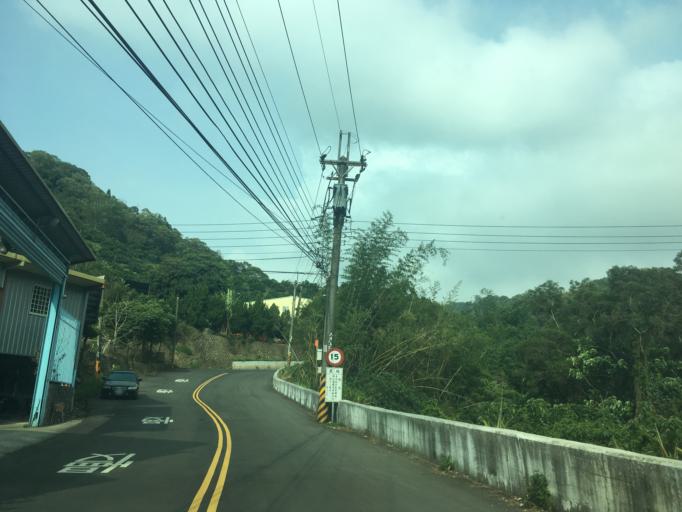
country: TW
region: Taiwan
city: Fengyuan
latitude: 24.2265
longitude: 120.7548
